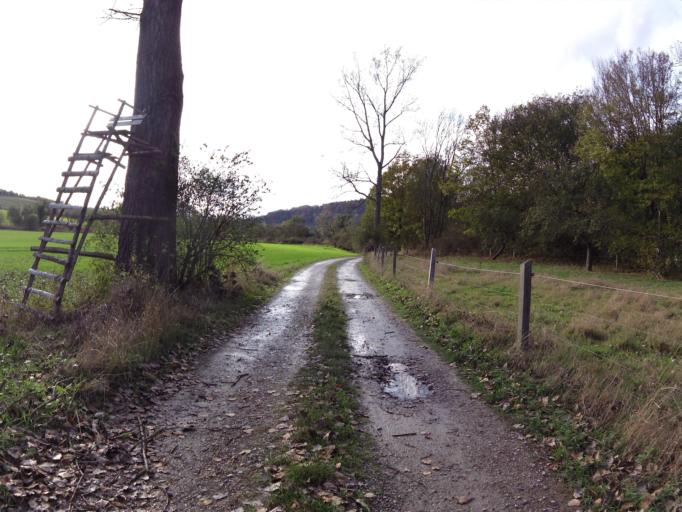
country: DE
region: Thuringia
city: Creuzburg
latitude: 51.0598
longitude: 10.2690
